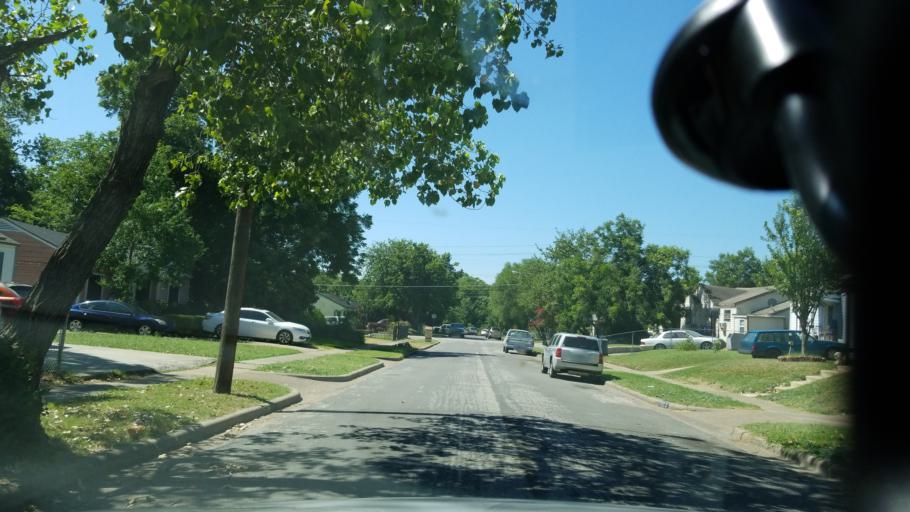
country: US
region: Texas
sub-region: Dallas County
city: Cockrell Hill
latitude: 32.7038
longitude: -96.8183
